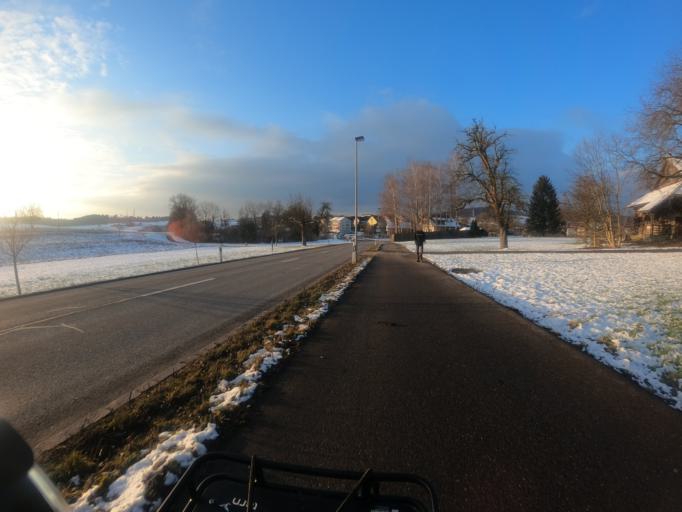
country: CH
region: Zurich
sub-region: Bezirk Affoltern
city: Affoltern / Unterdorf
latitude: 47.2859
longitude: 8.4418
